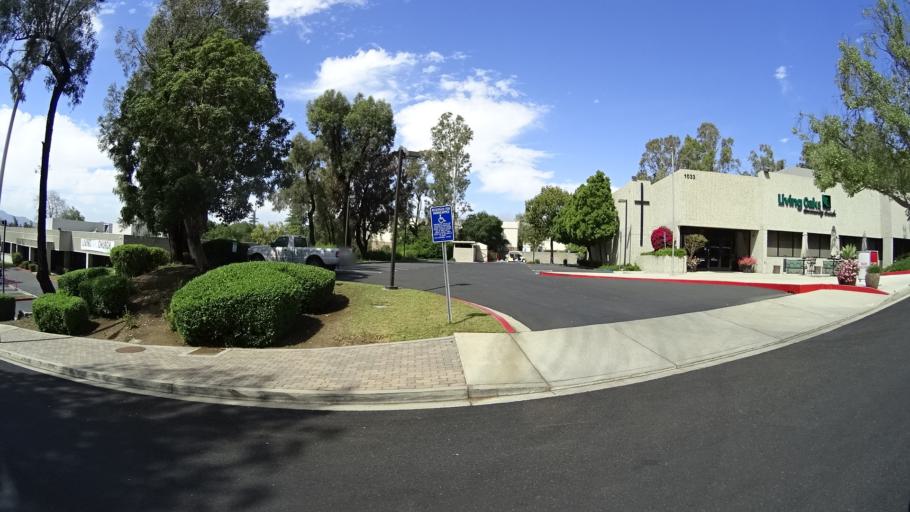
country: US
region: California
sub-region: Ventura County
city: Casa Conejo
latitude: 34.1930
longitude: -118.9427
